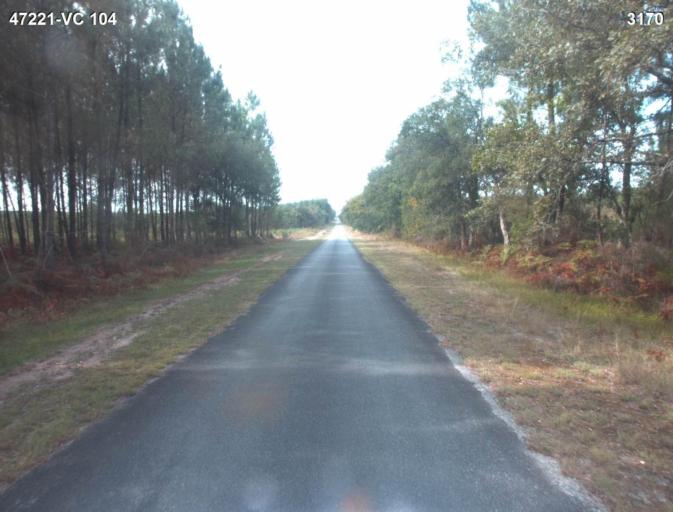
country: FR
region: Aquitaine
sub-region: Departement du Lot-et-Garonne
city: Mezin
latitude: 44.1239
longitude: 0.1894
